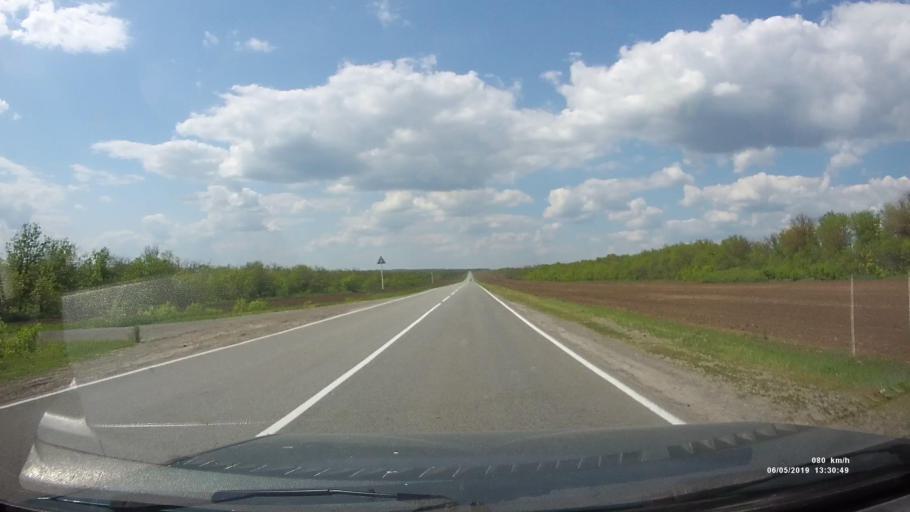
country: RU
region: Rostov
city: Ust'-Donetskiy
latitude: 47.6722
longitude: 40.8199
